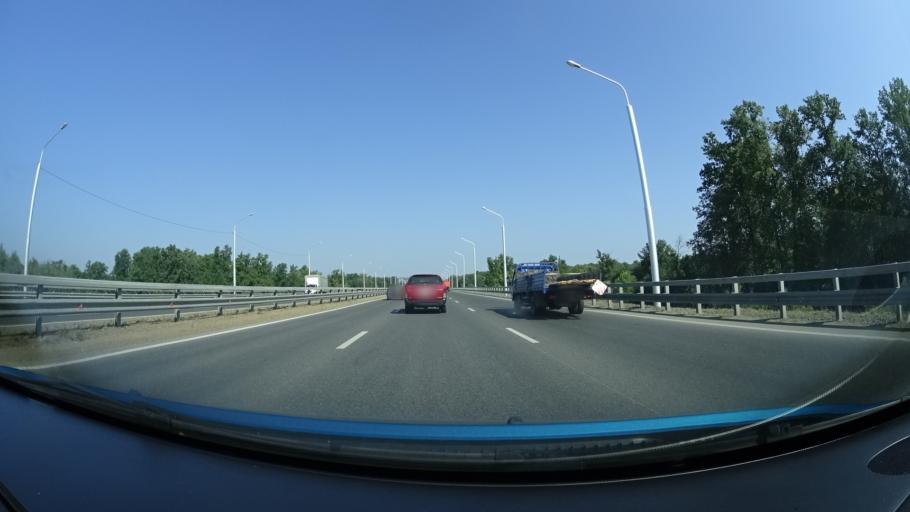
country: RU
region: Bashkortostan
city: Mikhaylovka
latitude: 54.7850
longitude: 55.9099
